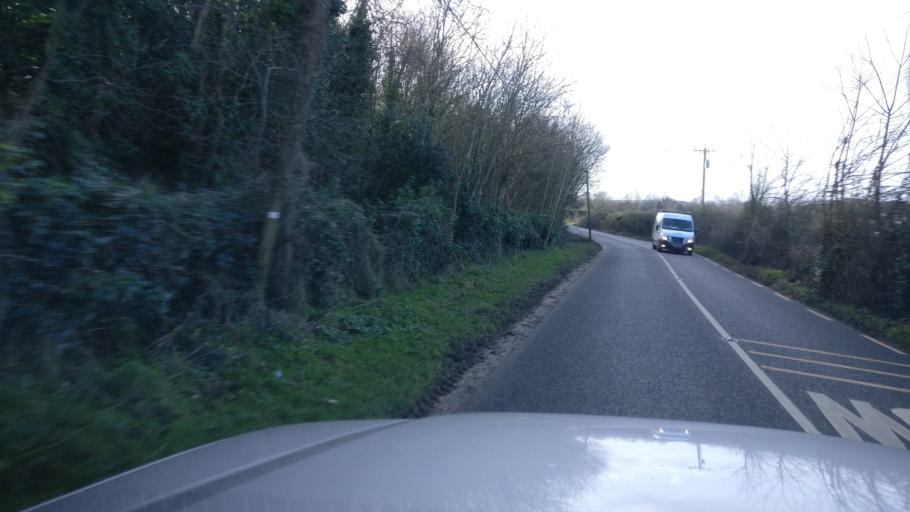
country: IE
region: Leinster
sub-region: Laois
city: Portlaoise
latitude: 53.0129
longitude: -7.2556
